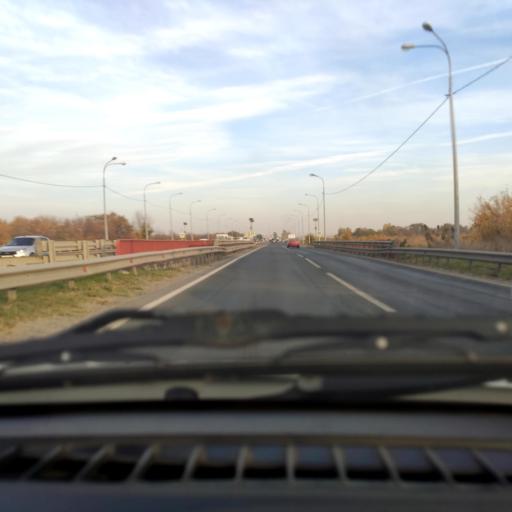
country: RU
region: Samara
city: Tol'yatti
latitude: 53.5740
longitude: 49.4502
